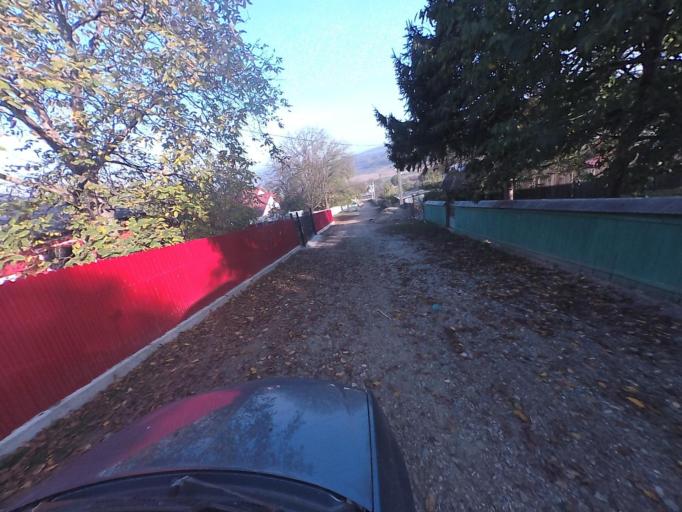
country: RO
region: Vaslui
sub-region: Comuna Bacesti
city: Bacesti
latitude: 46.8236
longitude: 27.2393
